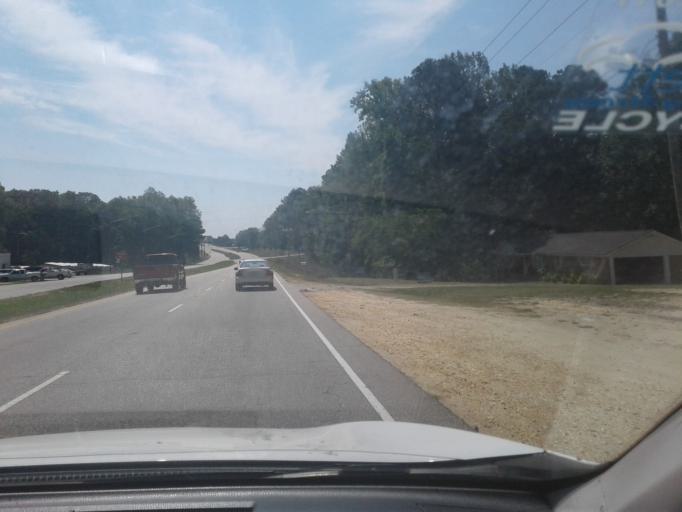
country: US
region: North Carolina
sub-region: Harnett County
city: Erwin
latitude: 35.3349
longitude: -78.6733
